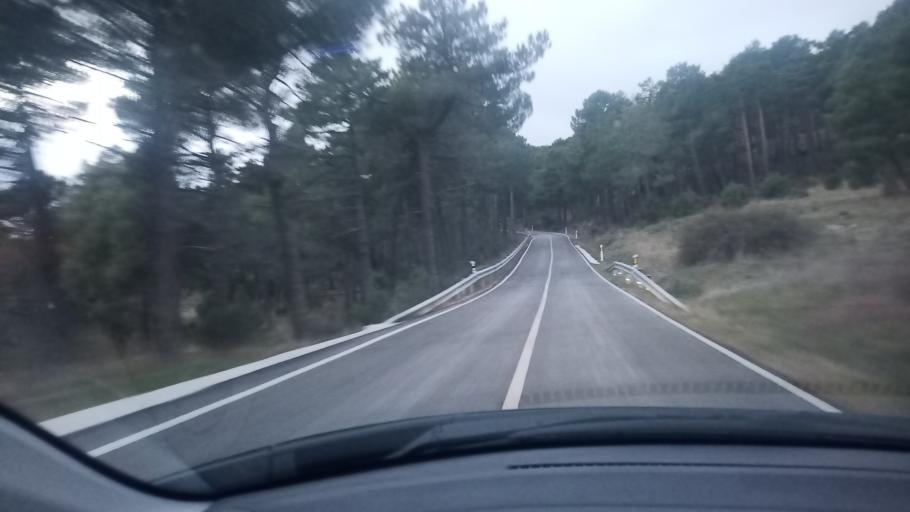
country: ES
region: Madrid
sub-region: Provincia de Madrid
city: Zarzalejo
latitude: 40.5556
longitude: -4.1882
